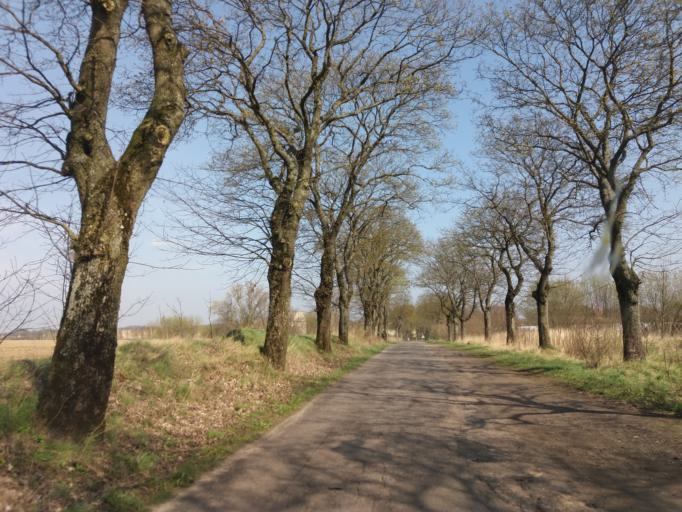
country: PL
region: West Pomeranian Voivodeship
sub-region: Powiat choszczenski
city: Recz
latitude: 53.2615
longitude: 15.6099
